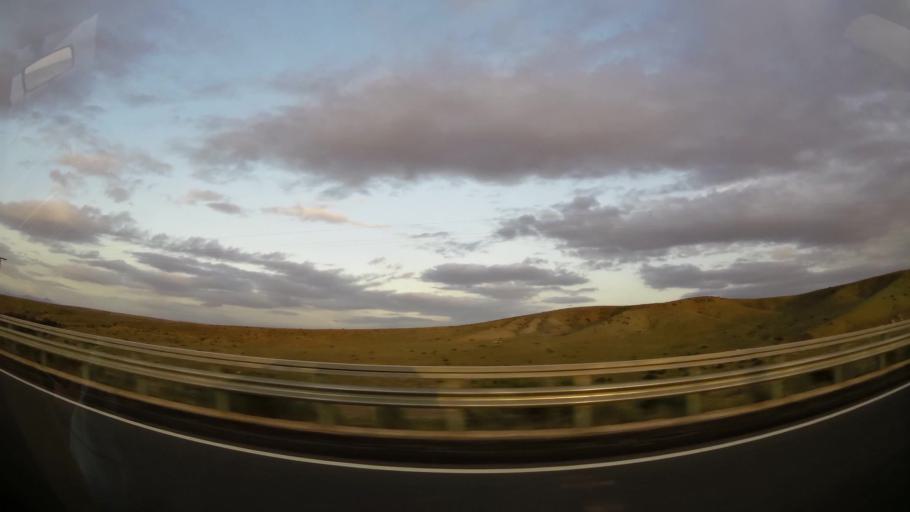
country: MA
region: Oriental
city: Taourirt
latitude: 34.5357
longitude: -2.9160
